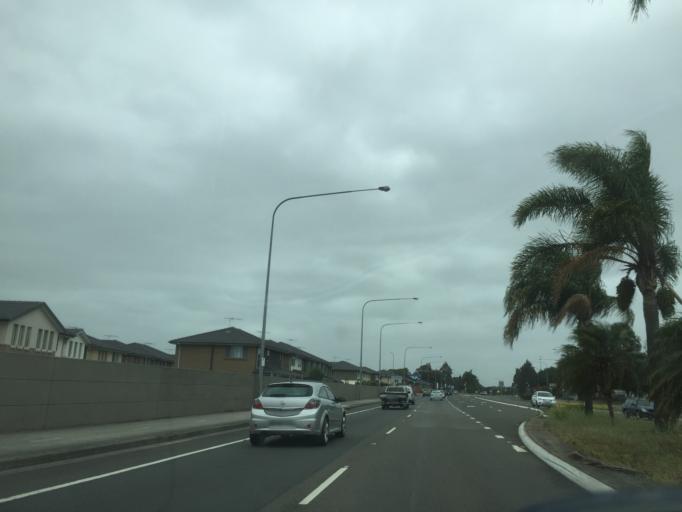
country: AU
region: New South Wales
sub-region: Blacktown
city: Stanhope Gardens
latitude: -33.7251
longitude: 150.9281
